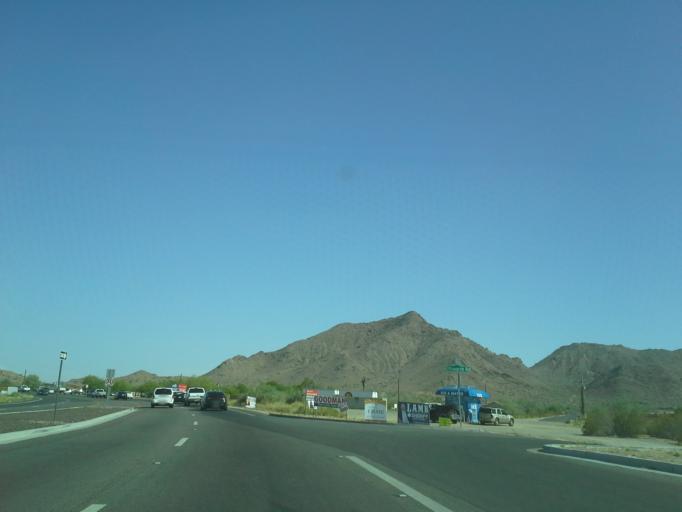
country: US
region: Arizona
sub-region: Maricopa County
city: Queen Creek
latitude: 33.2034
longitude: -111.6342
